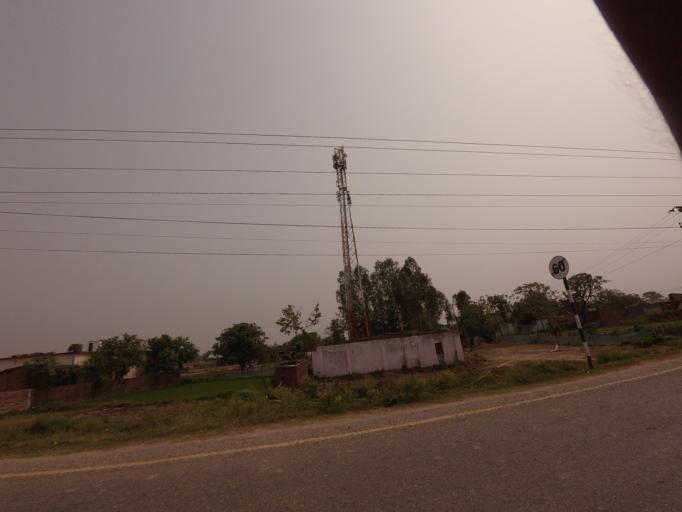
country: IN
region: Uttar Pradesh
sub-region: Maharajganj
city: Nautanwa
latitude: 27.4914
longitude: 83.3030
